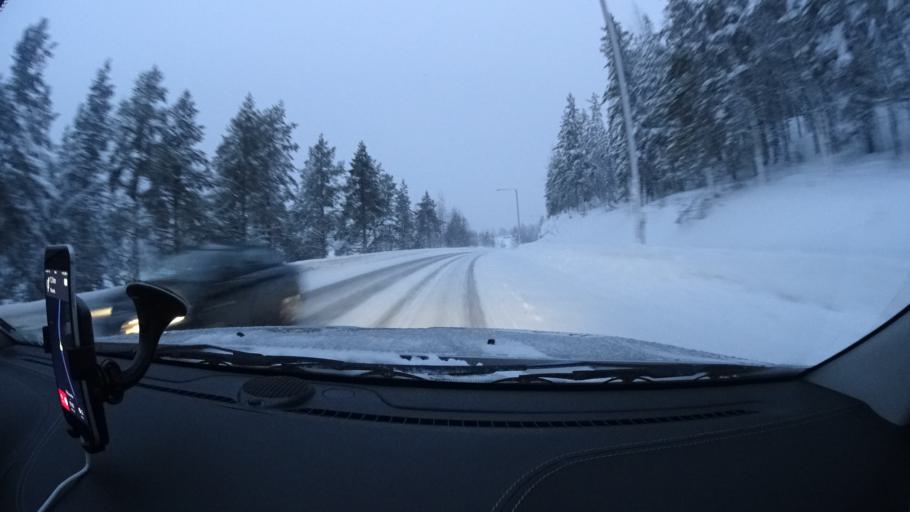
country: FI
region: Lapland
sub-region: Tunturi-Lappi
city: Kittilae
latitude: 67.7949
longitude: 24.7938
